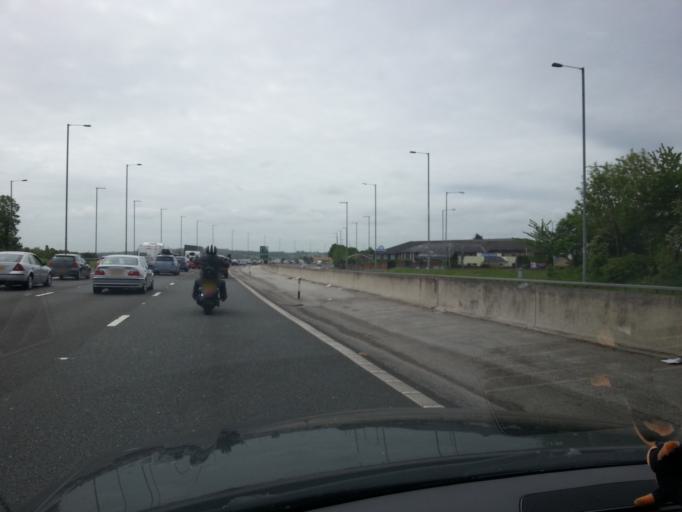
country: GB
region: England
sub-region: Cheshire West and Chester
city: Shotwick
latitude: 53.2164
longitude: -3.0017
